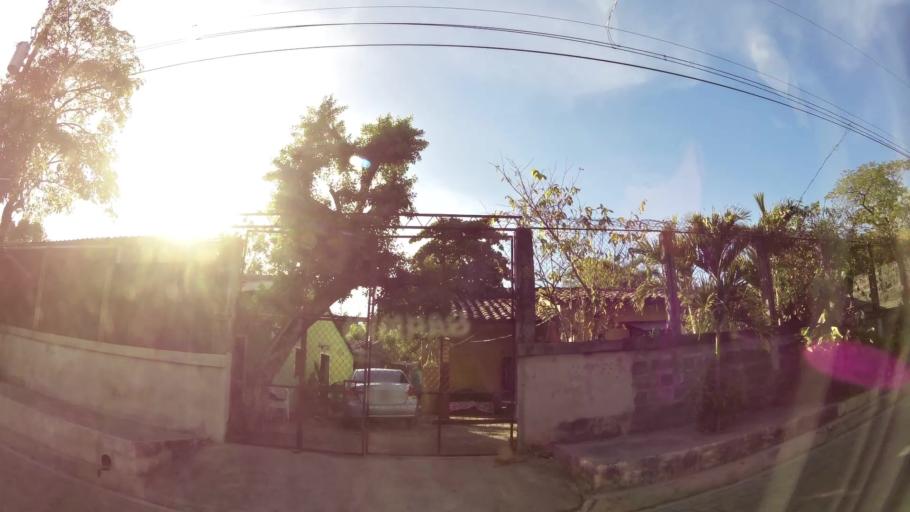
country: SV
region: San Miguel
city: San Miguel
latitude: 13.4634
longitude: -88.1817
